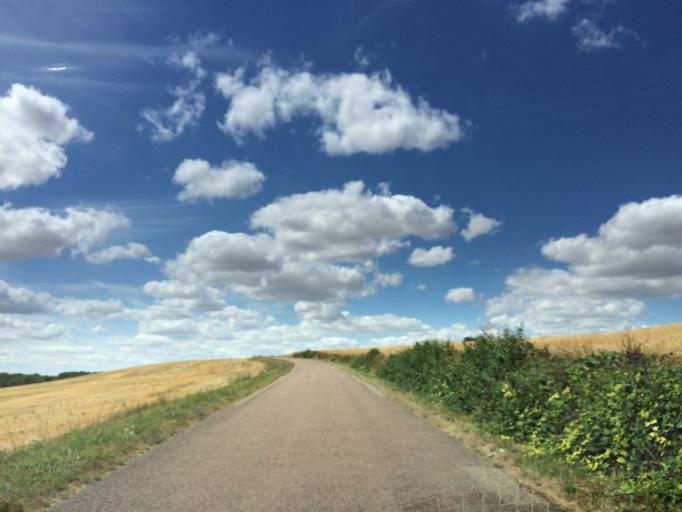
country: FR
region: Bourgogne
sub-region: Departement de l'Yonne
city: Fleury-la-Vallee
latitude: 47.8942
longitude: 3.4805
